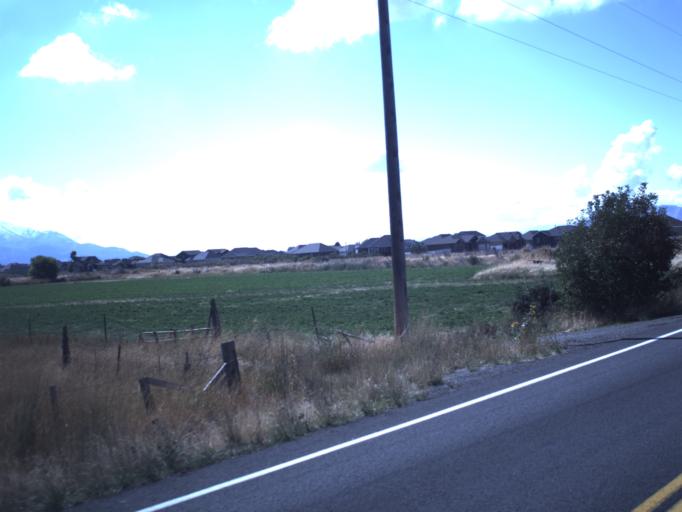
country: US
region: Utah
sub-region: Utah County
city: Spanish Fork
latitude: 40.1155
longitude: -111.6153
